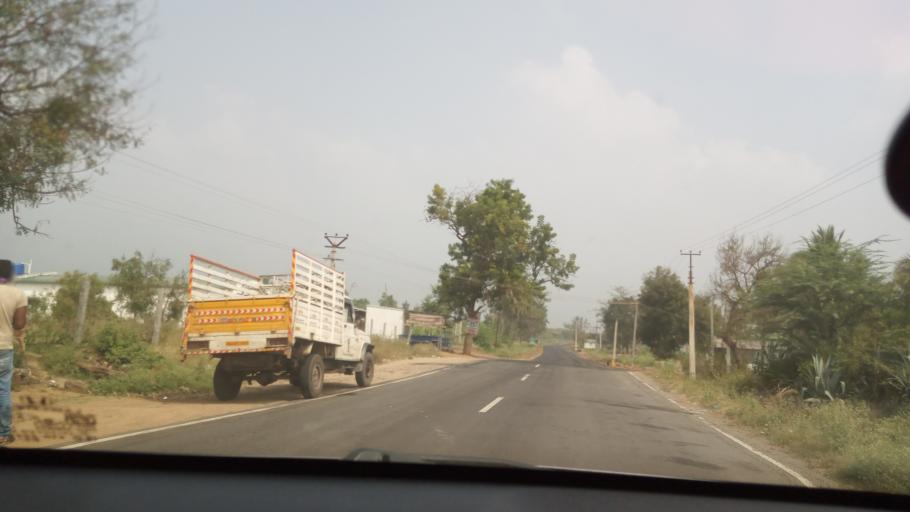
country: IN
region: Tamil Nadu
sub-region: Erode
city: Sathyamangalam
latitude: 11.5385
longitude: 77.1385
